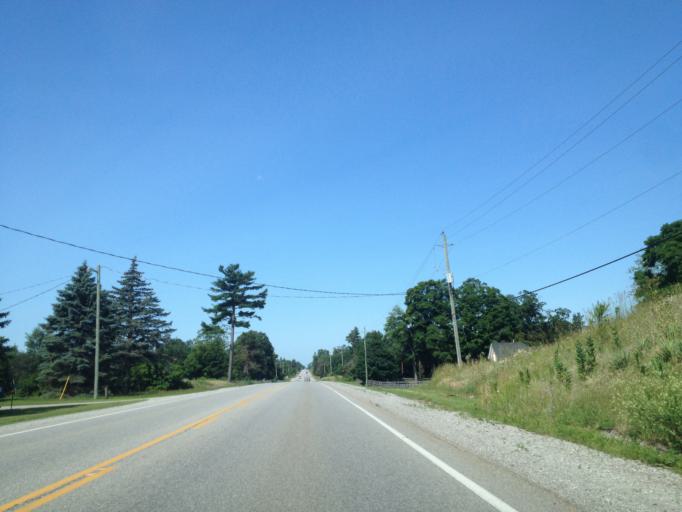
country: CA
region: Ontario
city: Norfolk County
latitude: 42.8364
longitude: -80.3602
